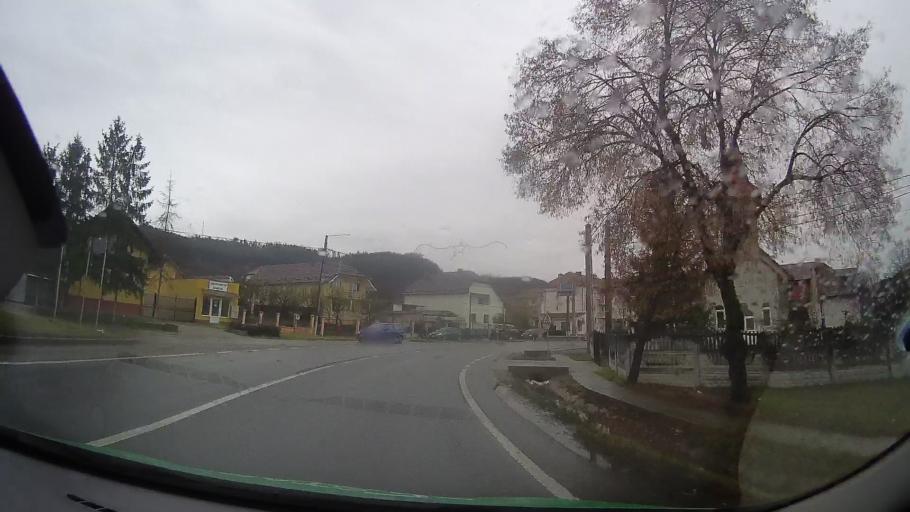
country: RO
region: Bistrita-Nasaud
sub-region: Comuna Teaca
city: Teaca
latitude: 46.9108
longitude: 24.5073
